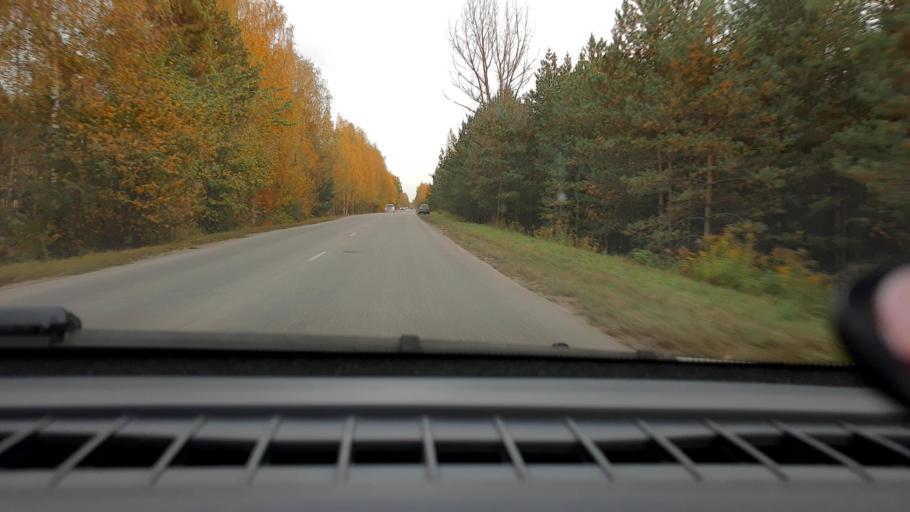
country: RU
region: Nizjnij Novgorod
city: Afonino
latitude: 56.3154
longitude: 44.1629
